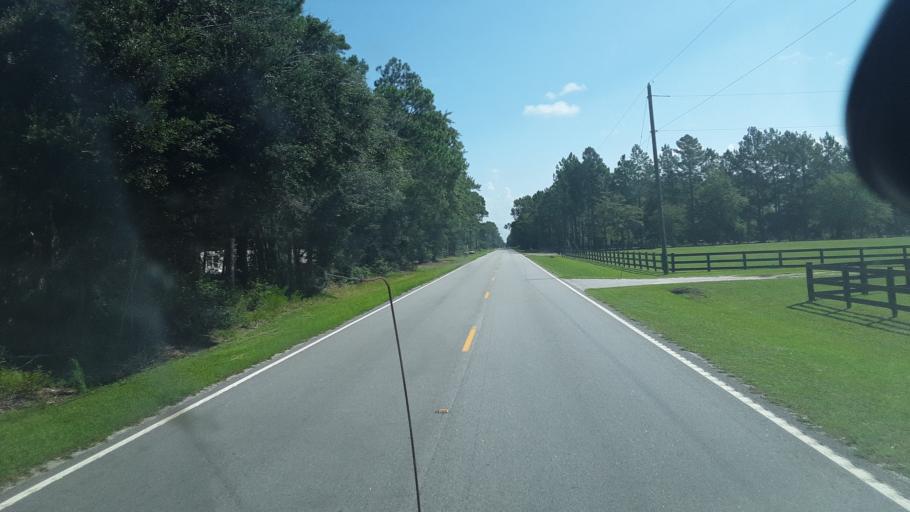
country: US
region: South Carolina
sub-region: Hampton County
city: Varnville
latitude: 32.8704
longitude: -81.0542
